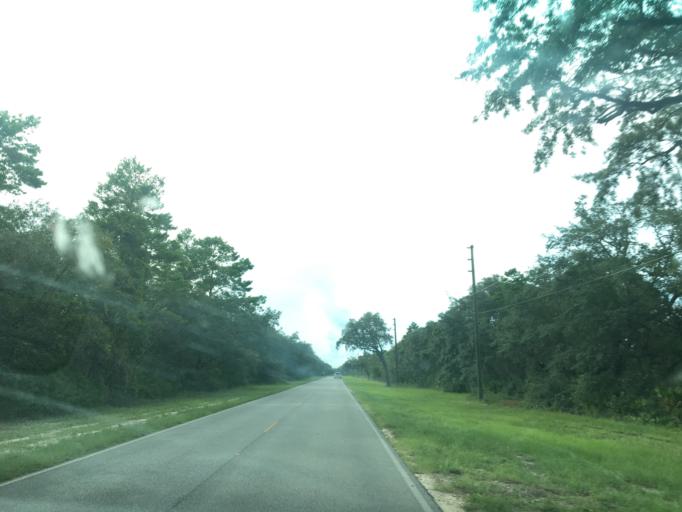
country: US
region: Florida
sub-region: Wakulla County
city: Crawfordville
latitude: 29.9042
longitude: -84.3522
